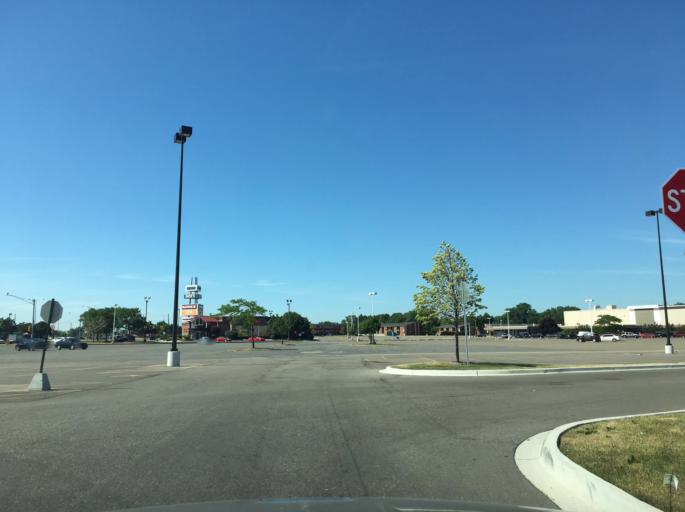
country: US
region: Michigan
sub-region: Macomb County
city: Fraser
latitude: 42.5346
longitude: -82.9136
